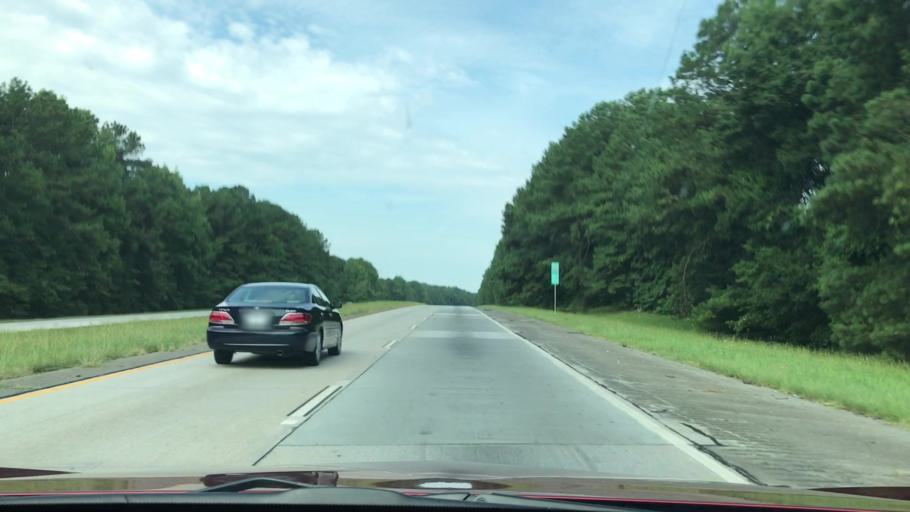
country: US
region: Georgia
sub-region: Warren County
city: Firing Range
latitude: 33.5025
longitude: -82.7748
